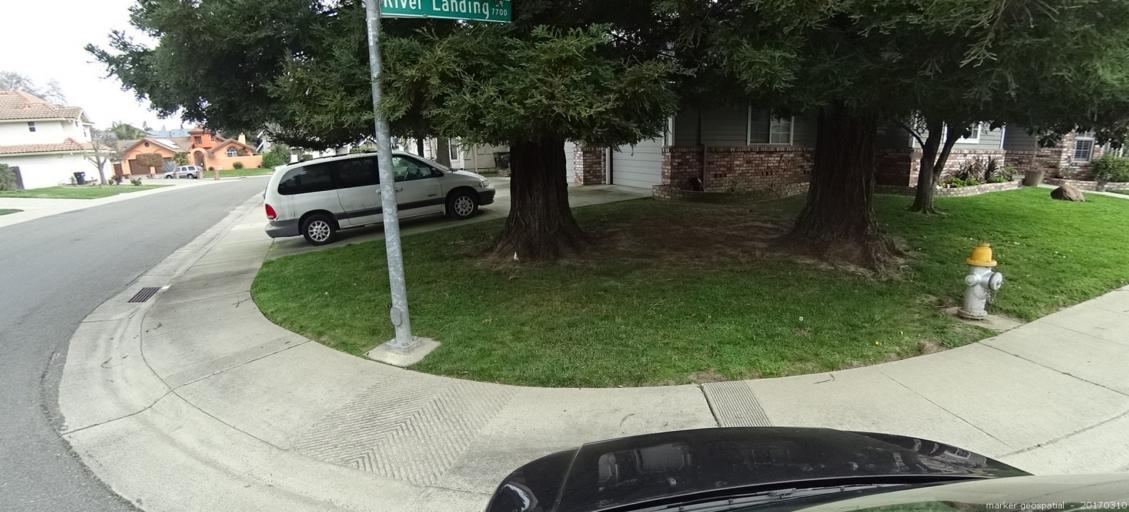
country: US
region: California
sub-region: Sacramento County
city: Parkway
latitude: 38.4769
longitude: -121.5396
